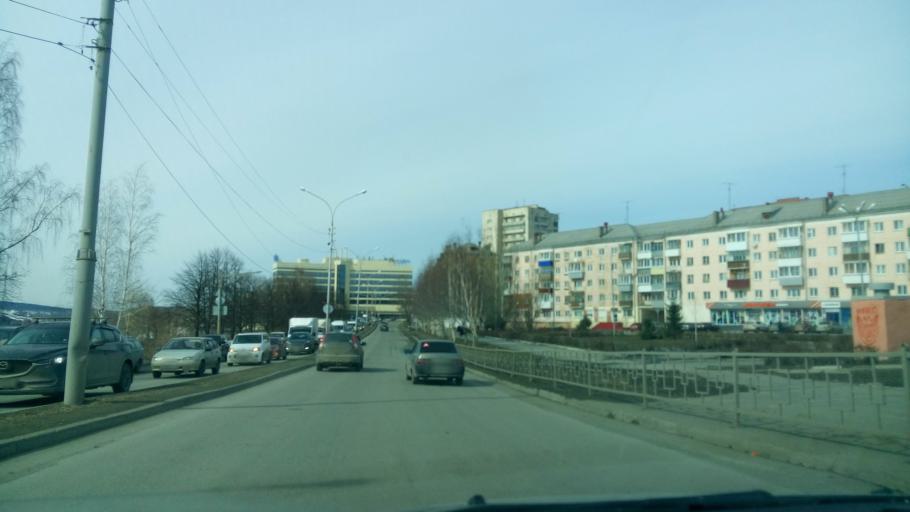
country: RU
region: Sverdlovsk
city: Nizhniy Tagil
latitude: 57.9046
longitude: 59.9896
